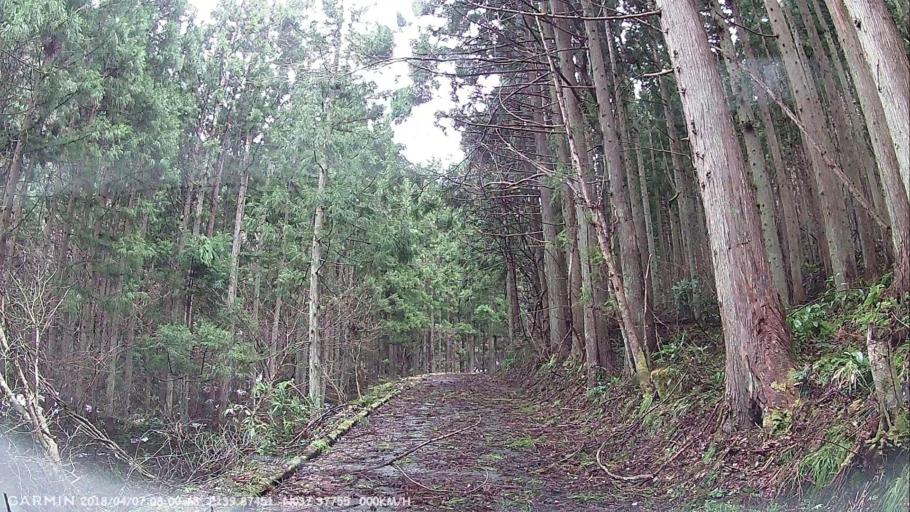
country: JP
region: Fukushima
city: Kitakata
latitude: 37.3776
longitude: 139.8745
